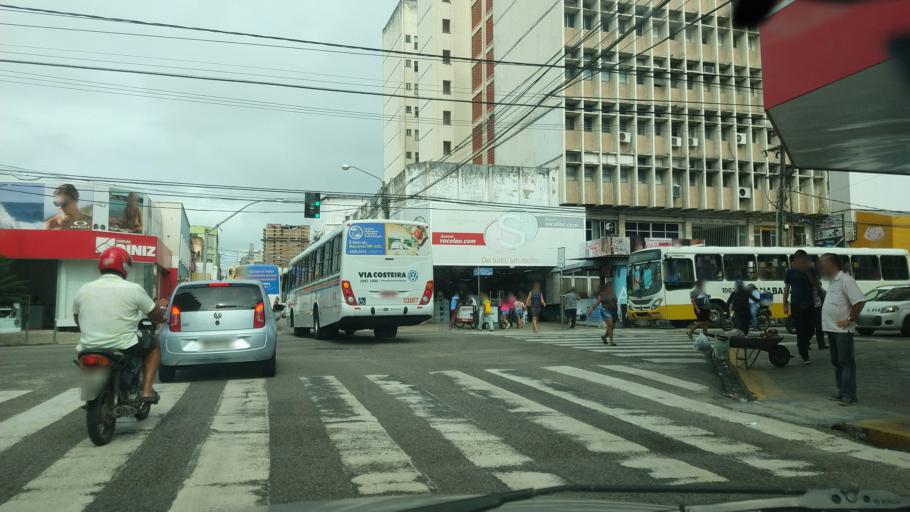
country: BR
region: Rio Grande do Norte
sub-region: Natal
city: Natal
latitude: -5.7850
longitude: -35.2065
